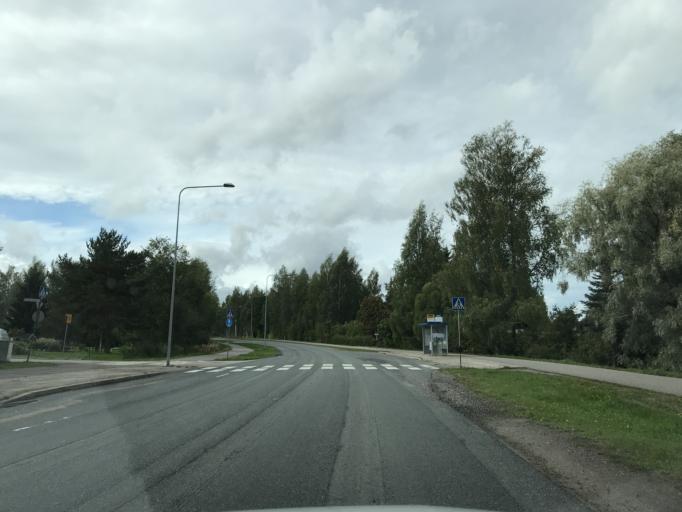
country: FI
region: Paijanne Tavastia
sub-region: Lahti
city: Lahti
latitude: 61.0118
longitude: 25.7888
